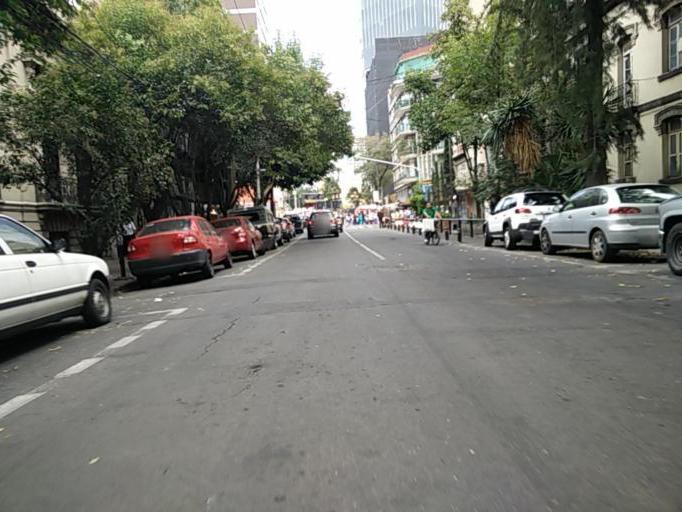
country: MX
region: Mexico City
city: Benito Juarez
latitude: 19.4219
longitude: -99.1621
